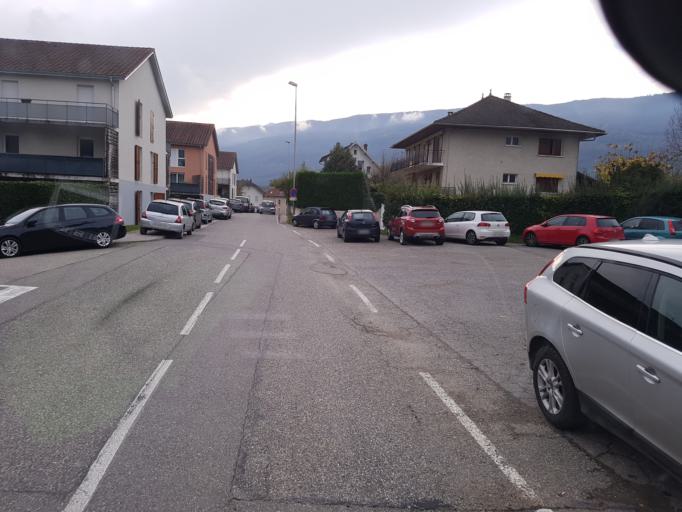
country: FR
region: Rhone-Alpes
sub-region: Departement de la Haute-Savoie
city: Versonnex
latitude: 45.9613
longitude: 5.8384
